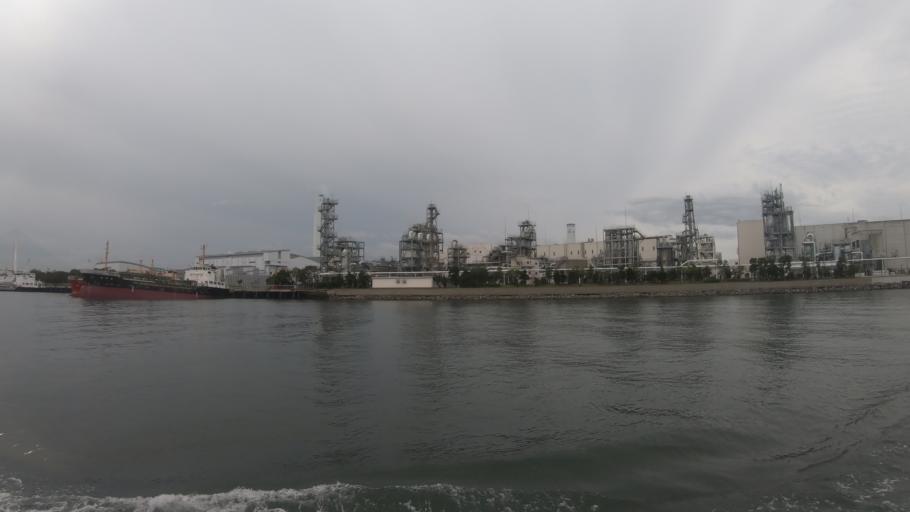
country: JP
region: Kanagawa
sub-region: Kawasaki-shi
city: Kawasaki
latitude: 35.4857
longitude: 139.6917
